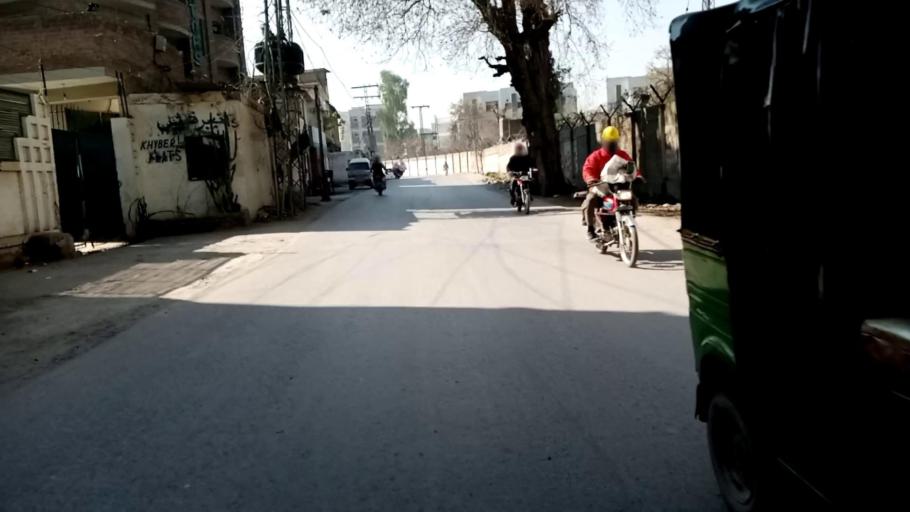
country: PK
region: Khyber Pakhtunkhwa
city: Peshawar
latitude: 33.9836
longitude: 71.5298
